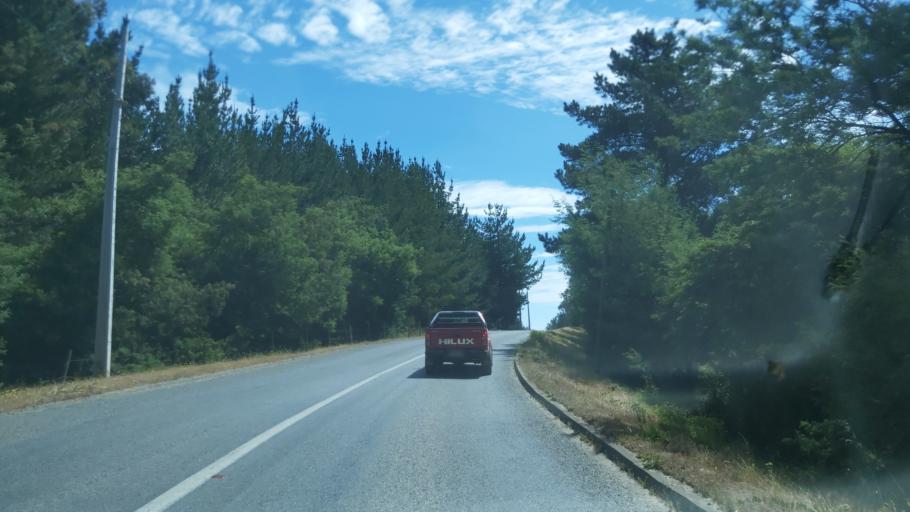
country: CL
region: Maule
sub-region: Provincia de Talca
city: Constitucion
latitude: -35.5510
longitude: -72.5694
